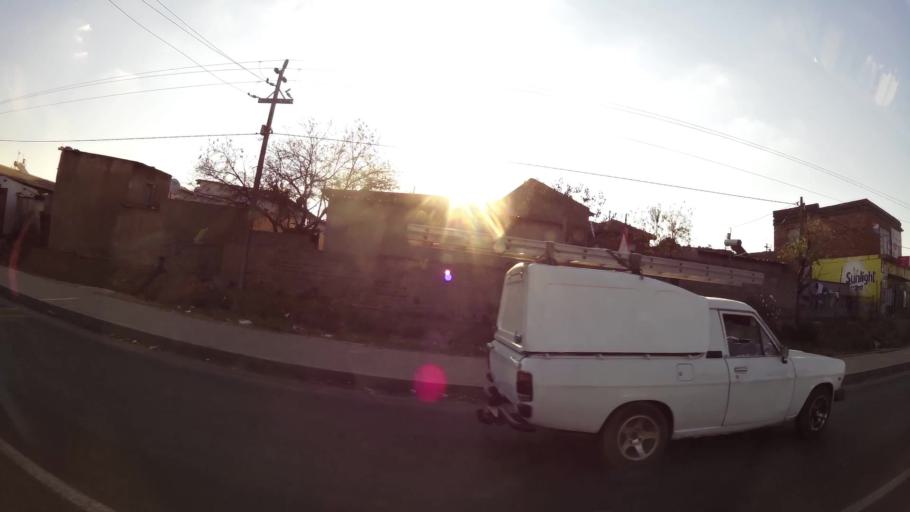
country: ZA
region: Gauteng
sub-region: Ekurhuleni Metropolitan Municipality
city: Tembisa
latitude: -26.0138
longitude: 28.1856
